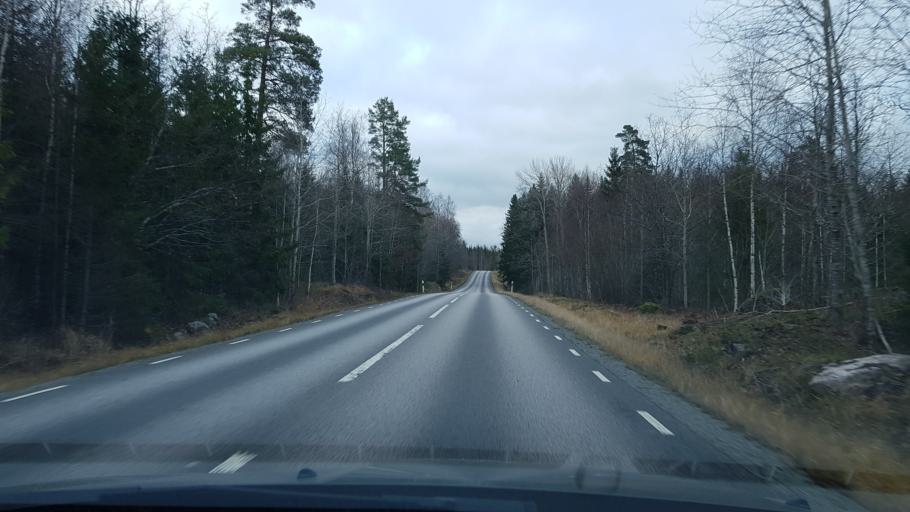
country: SE
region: Stockholm
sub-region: Norrtalje Kommun
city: Skanninge
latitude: 60.0313
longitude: 18.4392
